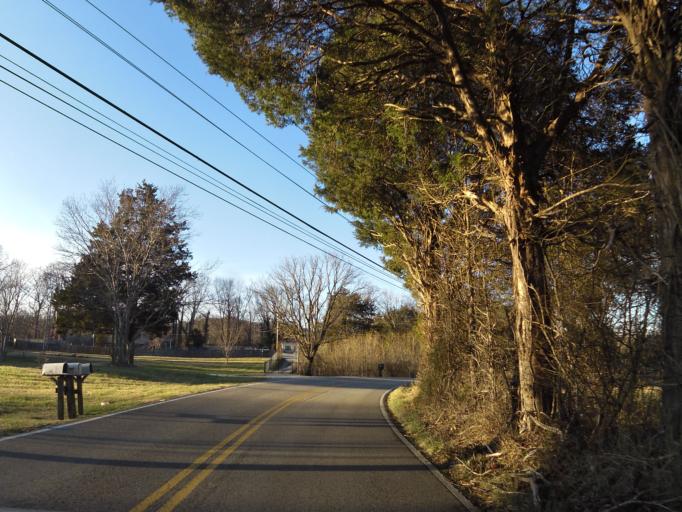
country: US
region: Tennessee
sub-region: Knox County
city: Farragut
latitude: 35.9450
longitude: -84.1268
